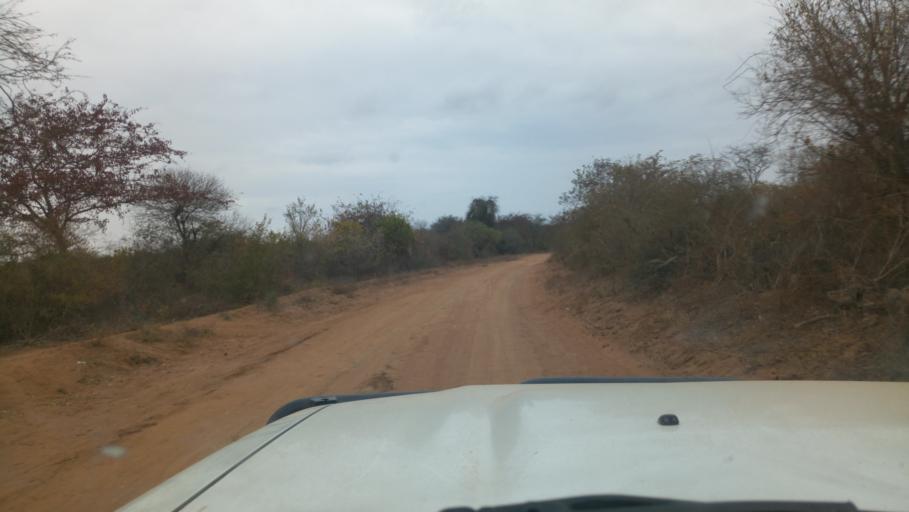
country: KE
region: Kitui
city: Kitui
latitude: -1.8734
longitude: 38.1667
